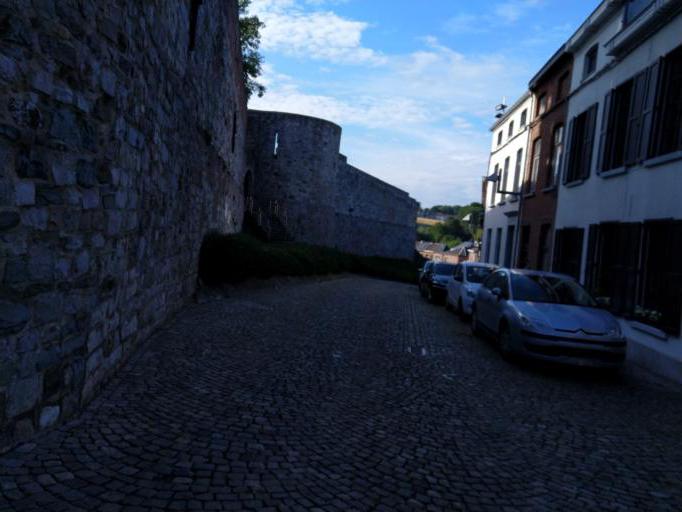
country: BE
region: Wallonia
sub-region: Province du Hainaut
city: Binche
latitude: 50.4089
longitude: 4.1639
